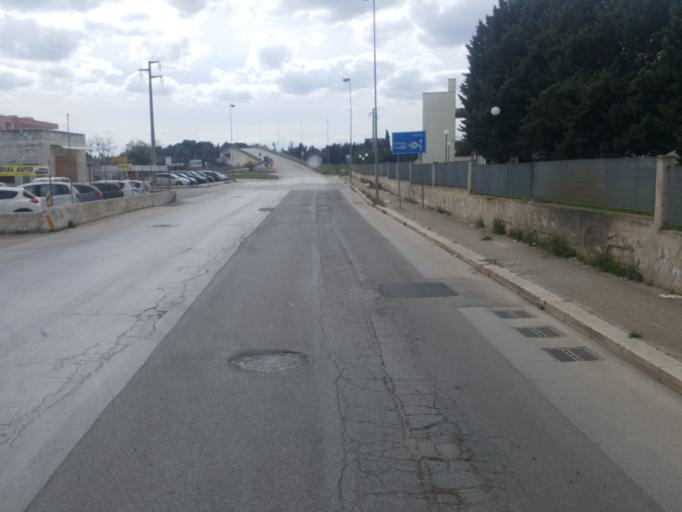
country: IT
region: Apulia
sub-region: Provincia di Barletta - Andria - Trani
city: Bisceglie
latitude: 41.2257
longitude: 16.5049
